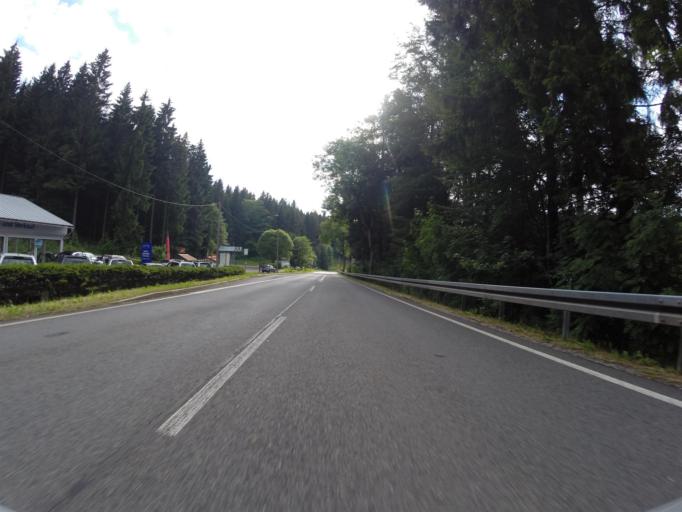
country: DE
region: Thuringia
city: Stutzerbach
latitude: 50.6284
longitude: 10.8506
